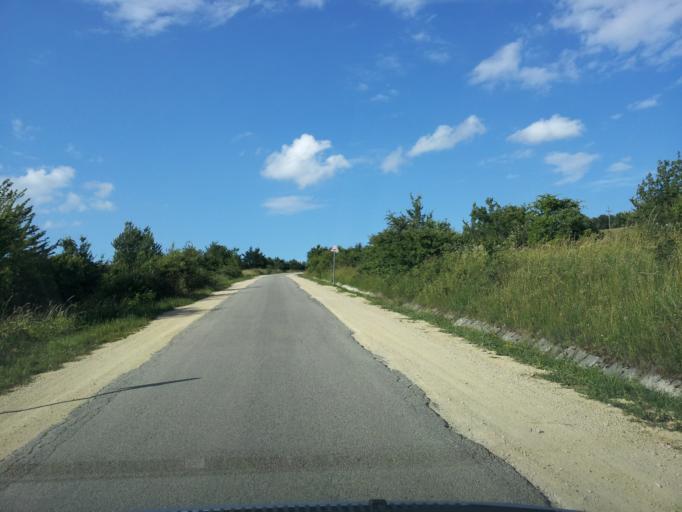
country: HU
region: Veszprem
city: Zirc
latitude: 47.1891
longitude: 17.8242
